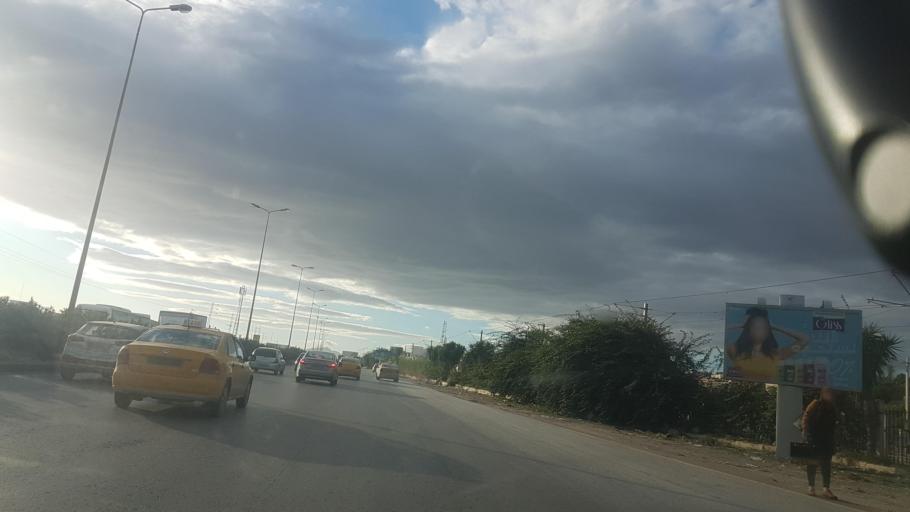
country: TN
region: Bin 'Arus
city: Ben Arous
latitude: 36.7542
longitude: 10.2026
